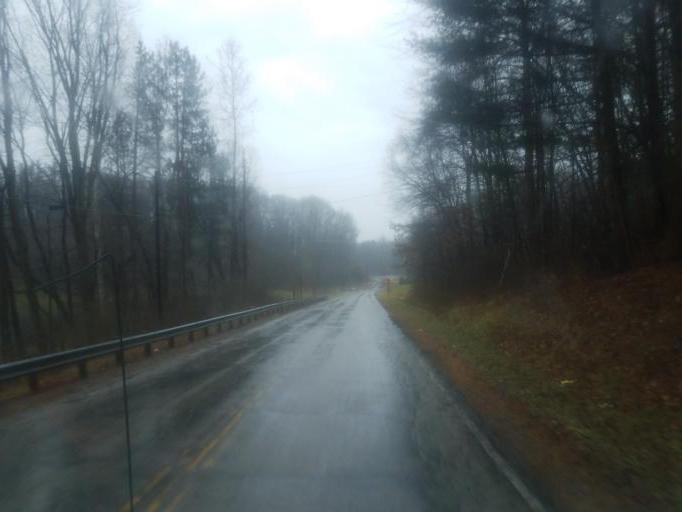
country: US
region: Ohio
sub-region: Sandusky County
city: Bellville
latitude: 40.6287
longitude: -82.5129
